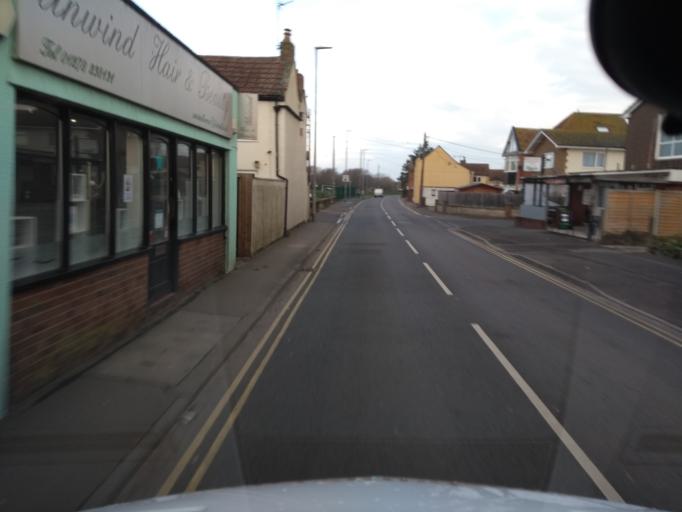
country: GB
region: England
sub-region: Somerset
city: Burnham-on-Sea
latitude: 51.2590
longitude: -3.0057
